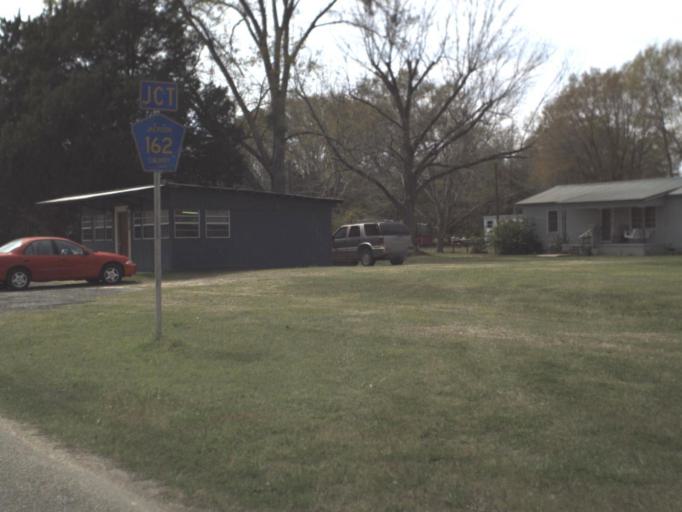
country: US
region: Florida
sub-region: Jackson County
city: Graceville
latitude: 30.8826
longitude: -85.5250
